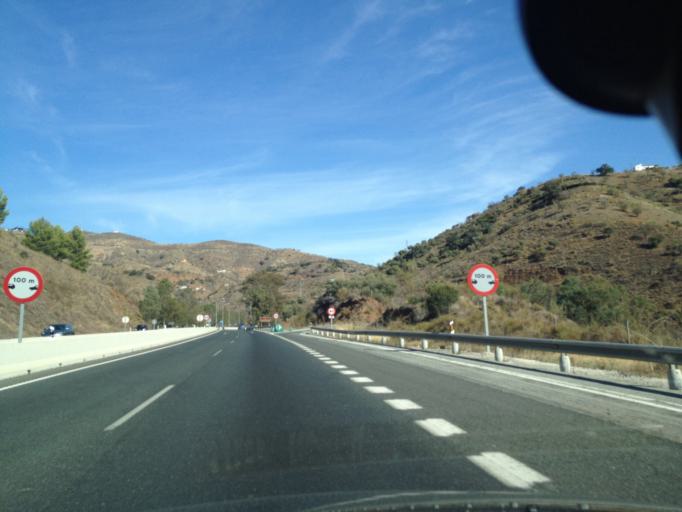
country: ES
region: Andalusia
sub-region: Provincia de Malaga
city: Casabermeja
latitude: 36.8668
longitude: -4.4359
